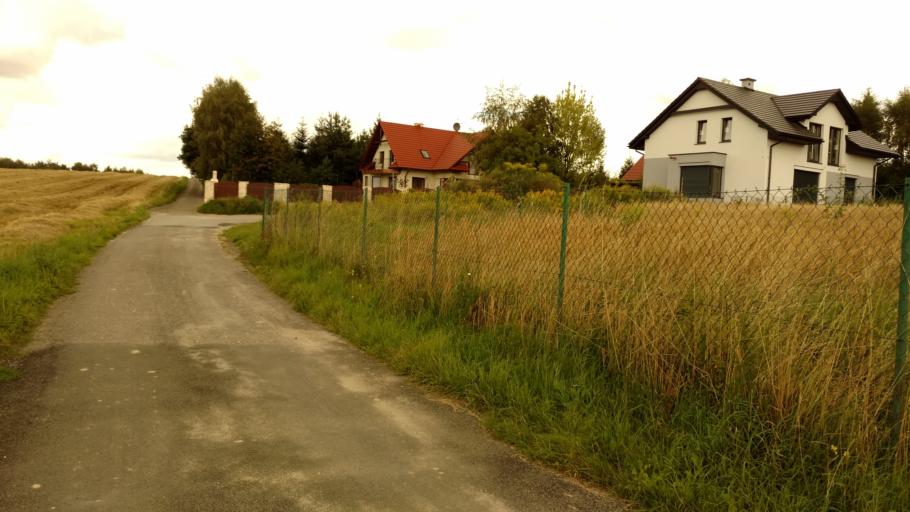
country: PL
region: Lesser Poland Voivodeship
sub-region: Powiat krakowski
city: Michalowice
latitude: 50.1355
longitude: 19.9617
